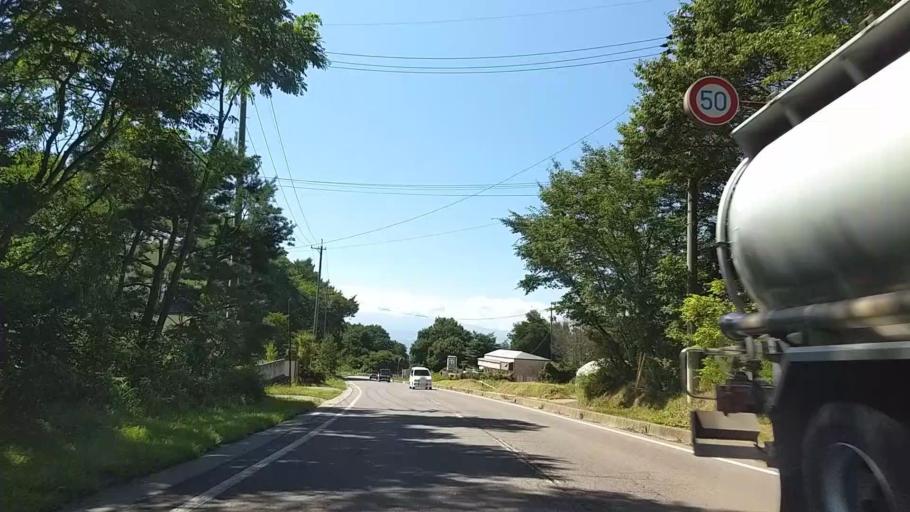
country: JP
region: Nagano
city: Komoro
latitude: 36.3372
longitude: 138.5160
